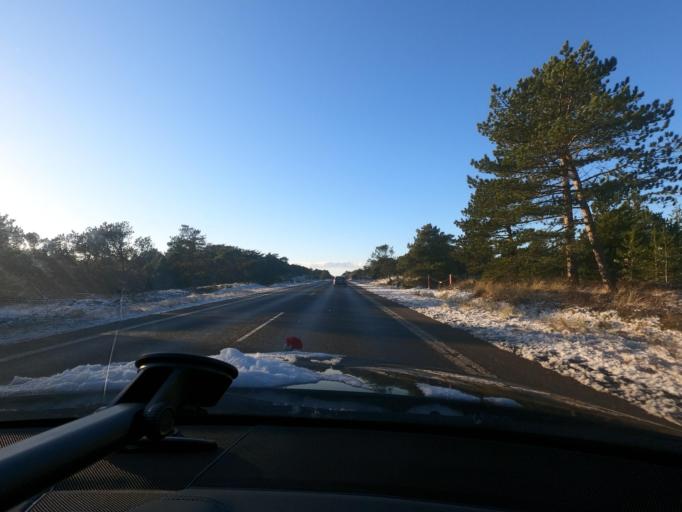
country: DE
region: Schleswig-Holstein
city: List
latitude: 55.1509
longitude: 8.5410
